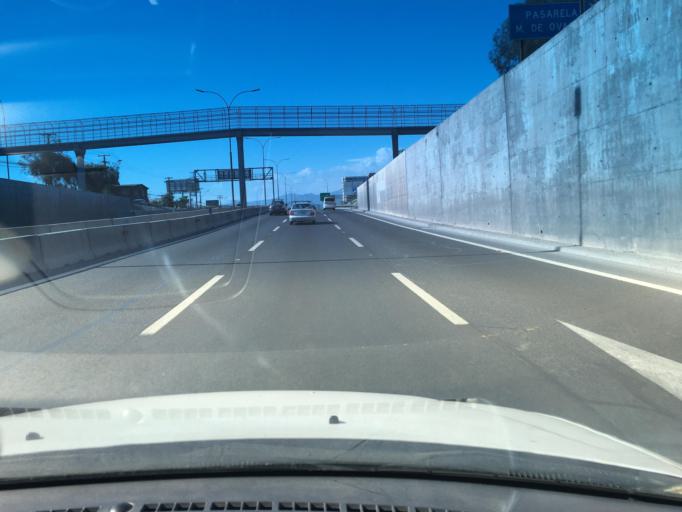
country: CL
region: Santiago Metropolitan
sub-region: Provincia de Santiago
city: Santiago
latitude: -33.4946
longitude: -70.6633
